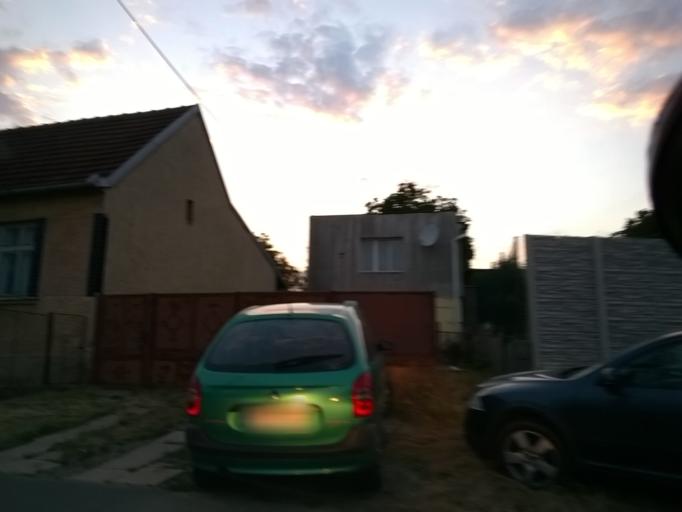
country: SK
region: Trnavsky
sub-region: Okres Senica
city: Senica
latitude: 48.7245
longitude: 17.3412
